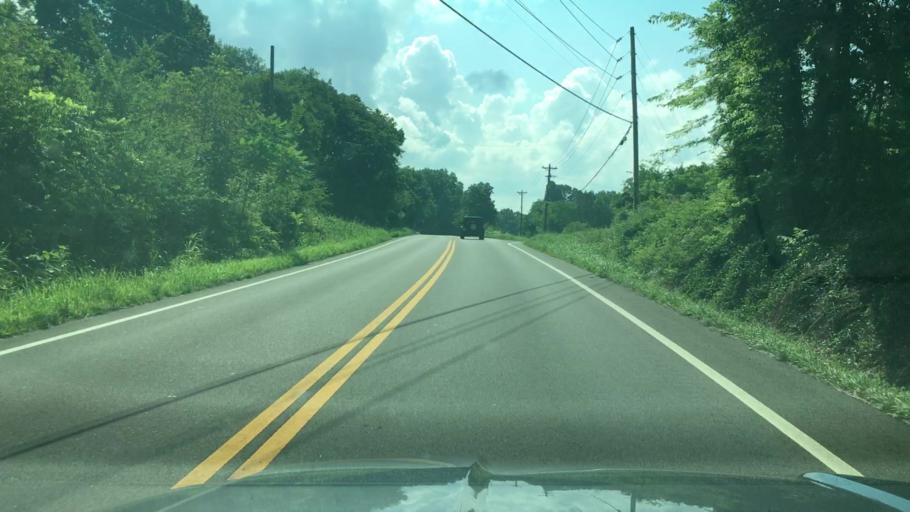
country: US
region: Tennessee
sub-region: Williamson County
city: Nolensville
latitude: 35.8718
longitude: -86.7282
